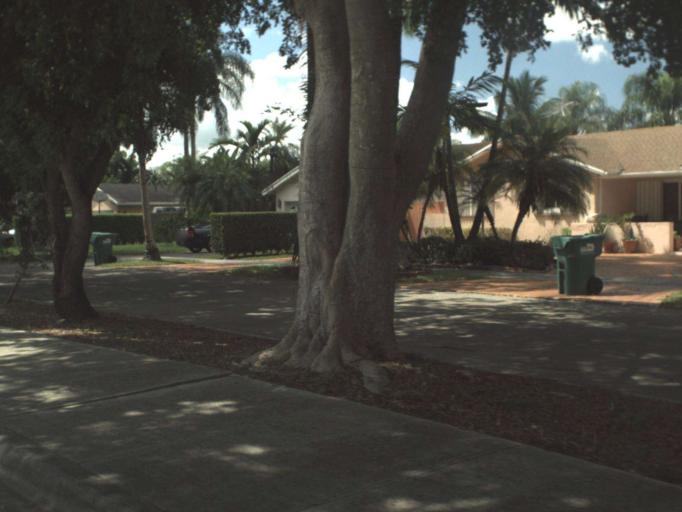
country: US
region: Florida
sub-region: Miami-Dade County
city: The Crossings
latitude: 25.6648
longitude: -80.4163
